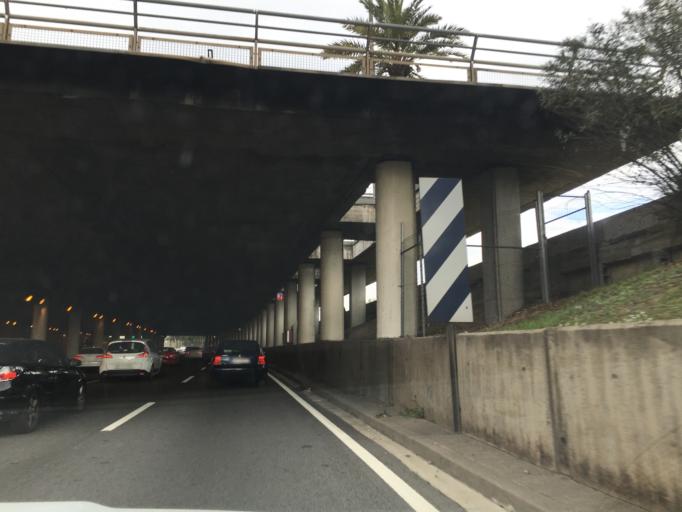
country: ES
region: Catalonia
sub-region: Provincia de Barcelona
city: Santa Coloma de Gramenet
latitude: 41.4469
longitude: 2.2034
